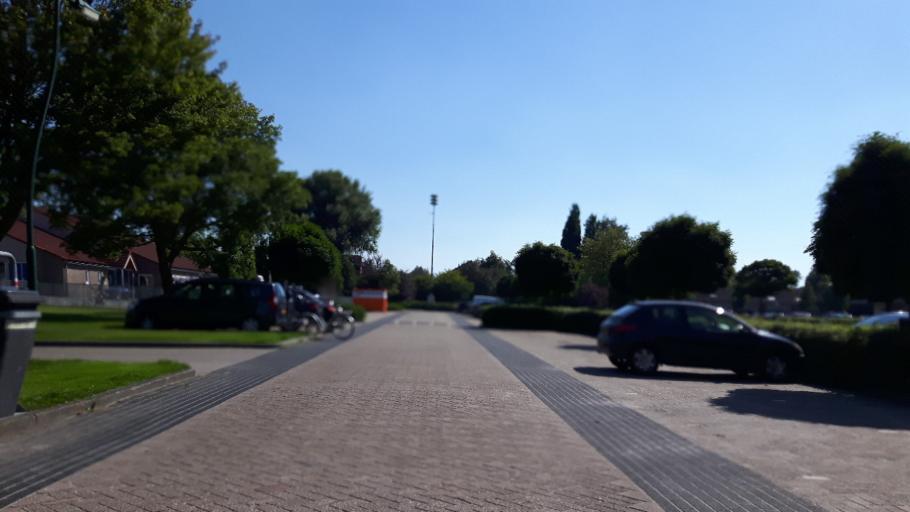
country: NL
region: Friesland
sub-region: Sudwest Fryslan
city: IJlst
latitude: 53.0119
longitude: 5.6261
